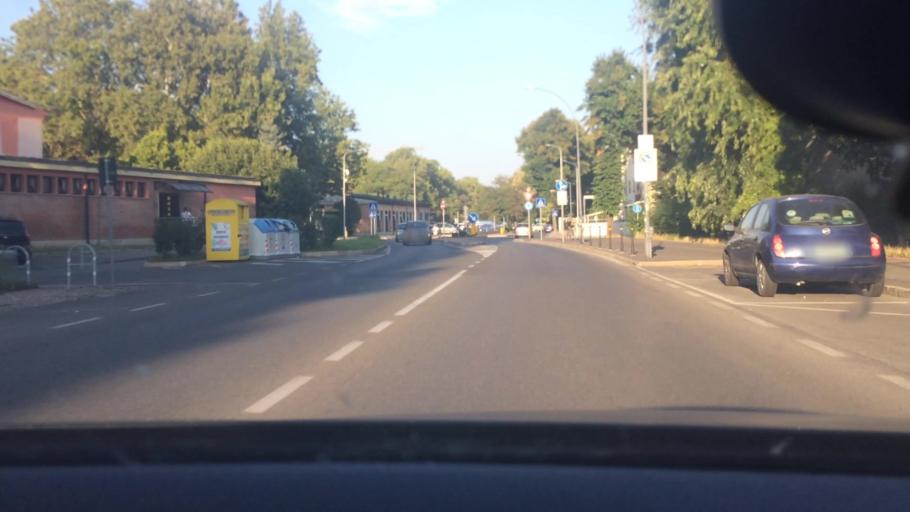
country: IT
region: Emilia-Romagna
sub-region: Provincia di Piacenza
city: Piacenza
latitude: 45.0449
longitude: 9.6904
